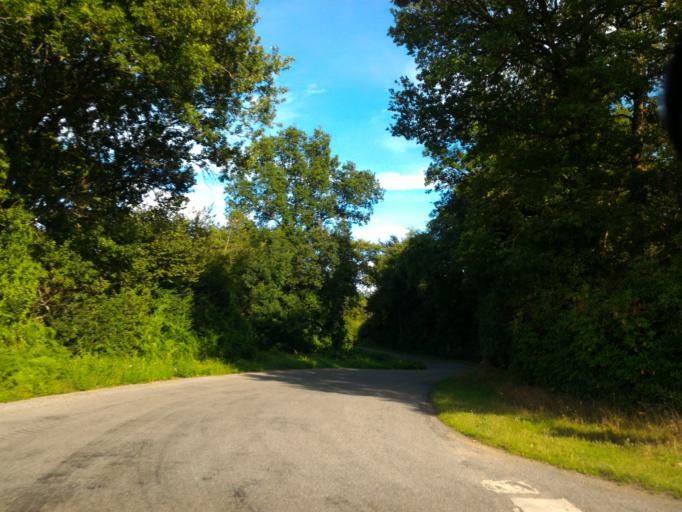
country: FR
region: Poitou-Charentes
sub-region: Departement de la Charente
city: Brigueuil
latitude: 45.9865
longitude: 0.8992
